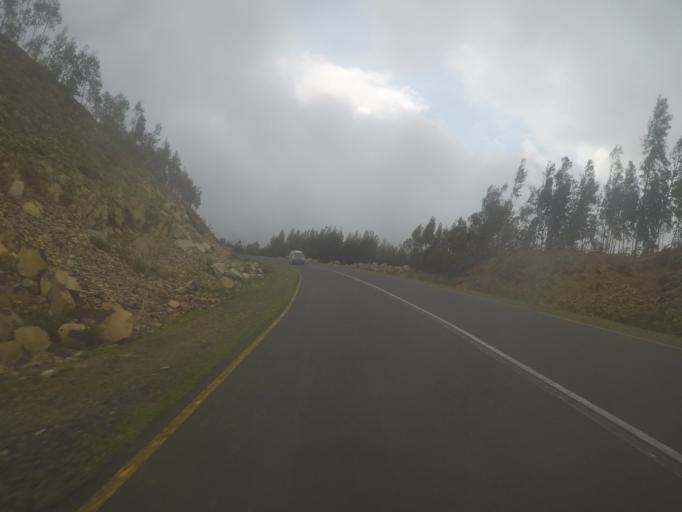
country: ET
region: Amhara
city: Gondar
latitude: 12.7306
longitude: 37.5168
